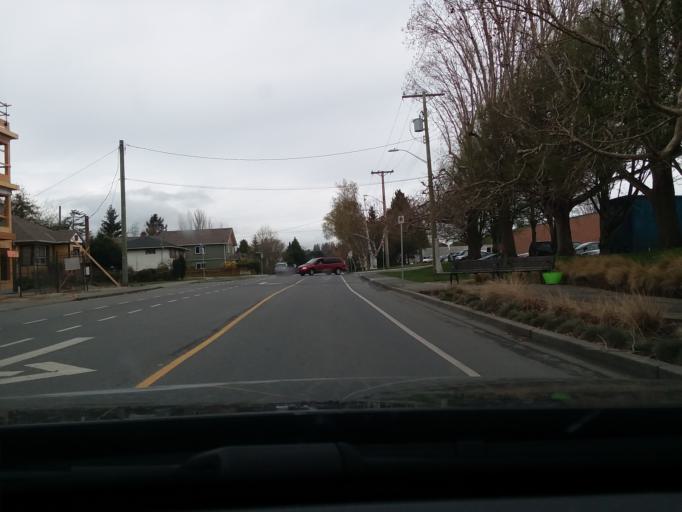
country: CA
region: British Columbia
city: Victoria
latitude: 48.4441
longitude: -123.3385
